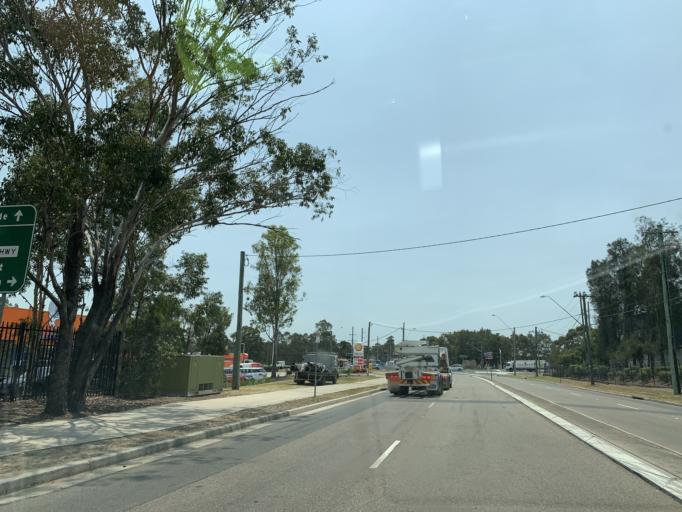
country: AU
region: New South Wales
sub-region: Blacktown
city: Doonside
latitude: -33.7939
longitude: 150.8713
